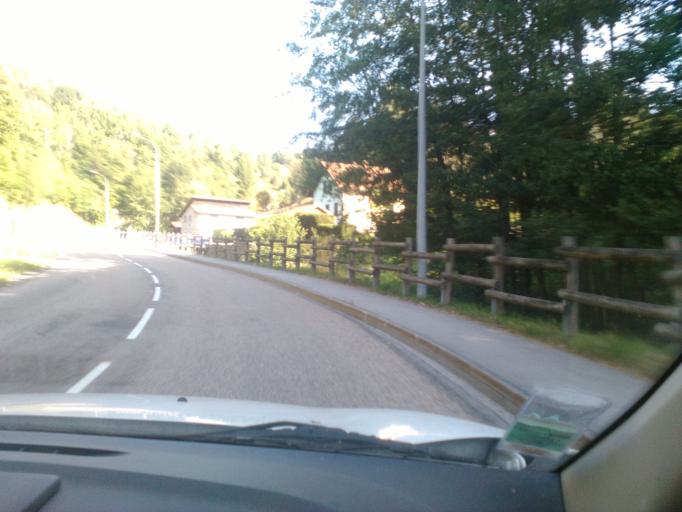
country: FR
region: Lorraine
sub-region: Departement des Vosges
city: La Bresse
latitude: 48.0127
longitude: 6.8893
